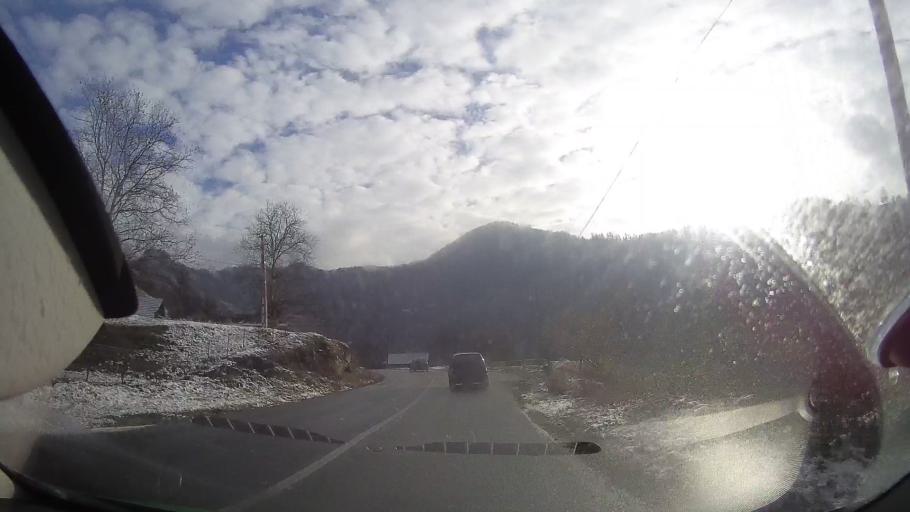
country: RO
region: Alba
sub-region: Oras Baia de Aries
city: Baia de Aries
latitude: 46.3908
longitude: 23.2906
